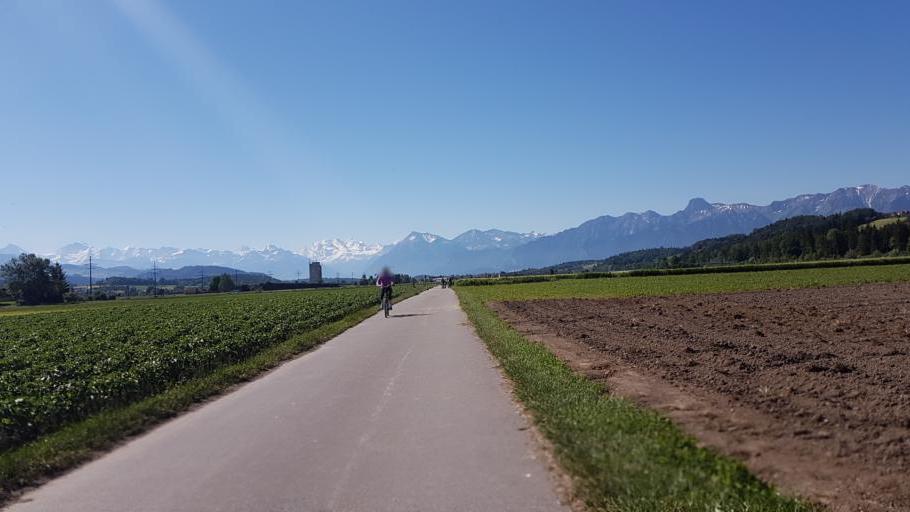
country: CH
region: Bern
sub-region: Bern-Mittelland District
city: Munsingen
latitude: 46.8557
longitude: 7.5608
